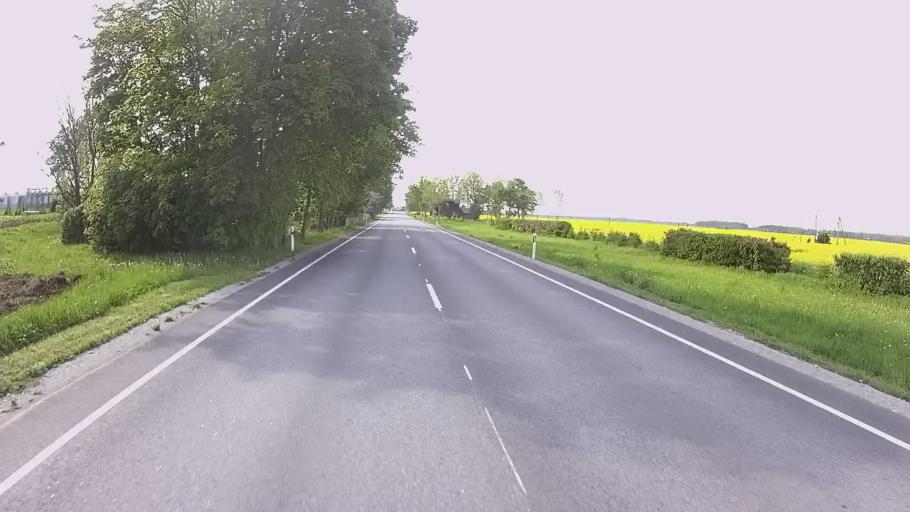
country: EE
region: Laeaene-Virumaa
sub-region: Vinni vald
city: Vinni
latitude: 59.2326
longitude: 26.5077
